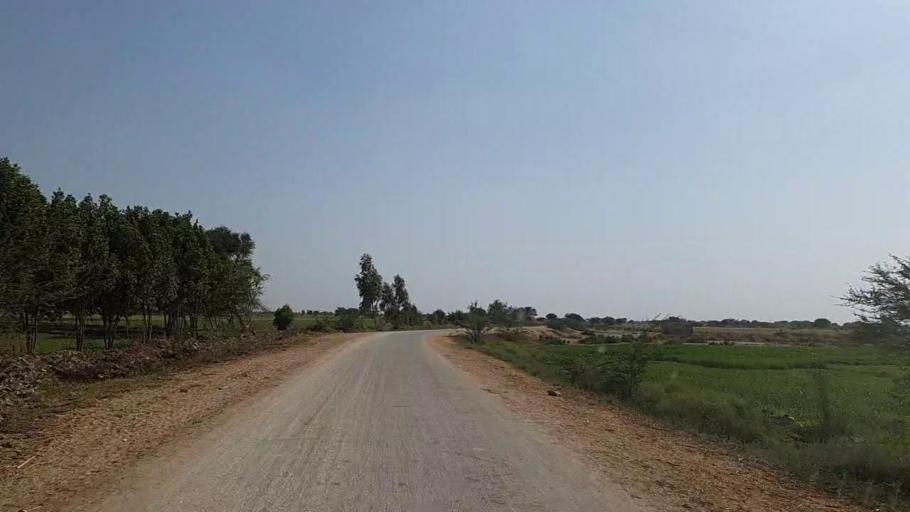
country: PK
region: Sindh
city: Daro Mehar
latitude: 24.7860
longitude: 68.1803
